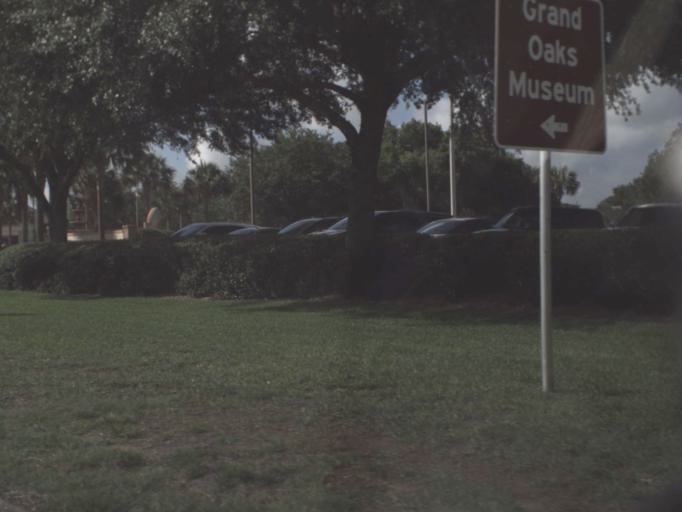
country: US
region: Florida
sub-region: Sumter County
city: The Villages
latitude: 28.9377
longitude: -81.9423
